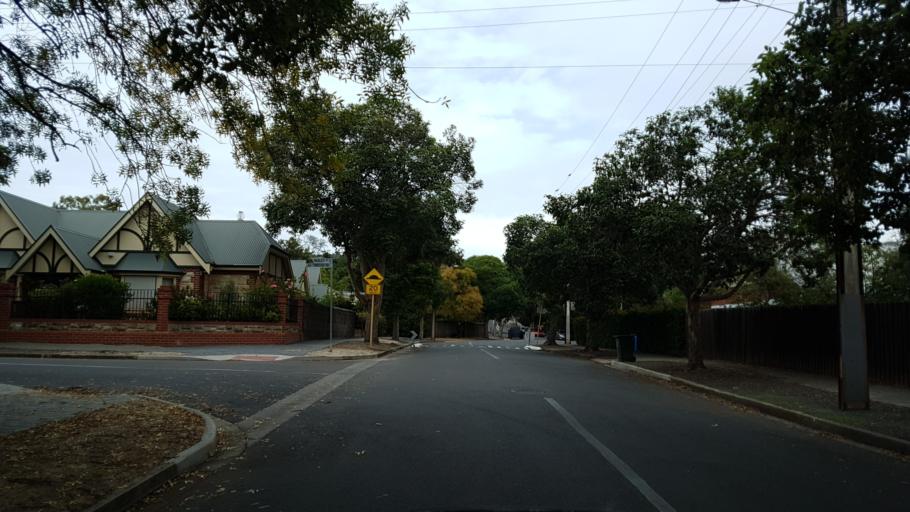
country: AU
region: South Australia
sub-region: Mitcham
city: Mitcham
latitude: -34.9788
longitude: 138.6143
